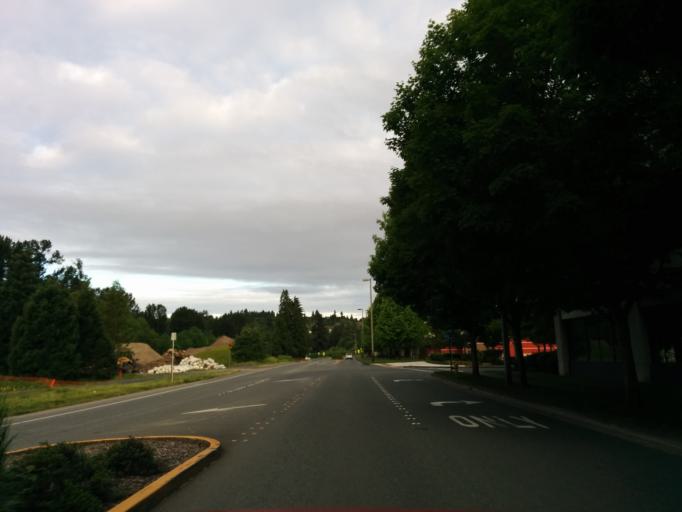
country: US
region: Washington
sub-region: King County
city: Redmond
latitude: 47.6685
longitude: -122.1181
